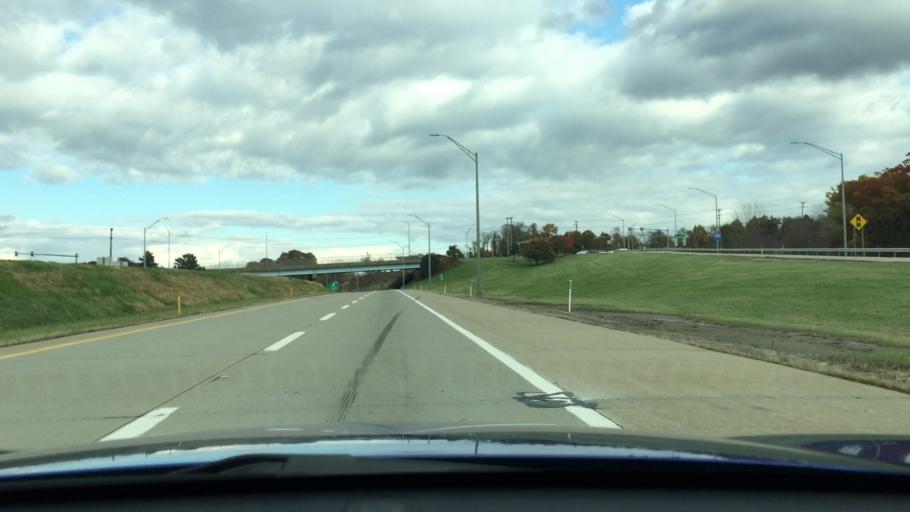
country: US
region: Pennsylvania
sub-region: Westmoreland County
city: Jeannette
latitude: 40.3064
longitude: -79.5989
